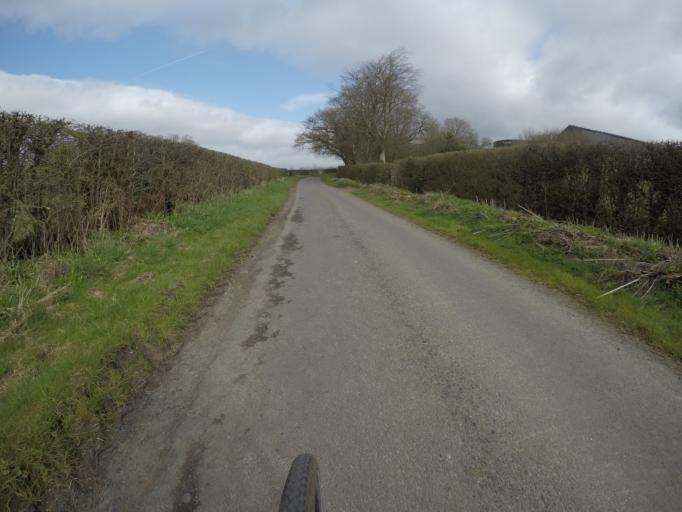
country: GB
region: Scotland
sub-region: North Ayrshire
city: Springside
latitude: 55.6489
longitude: -4.6175
